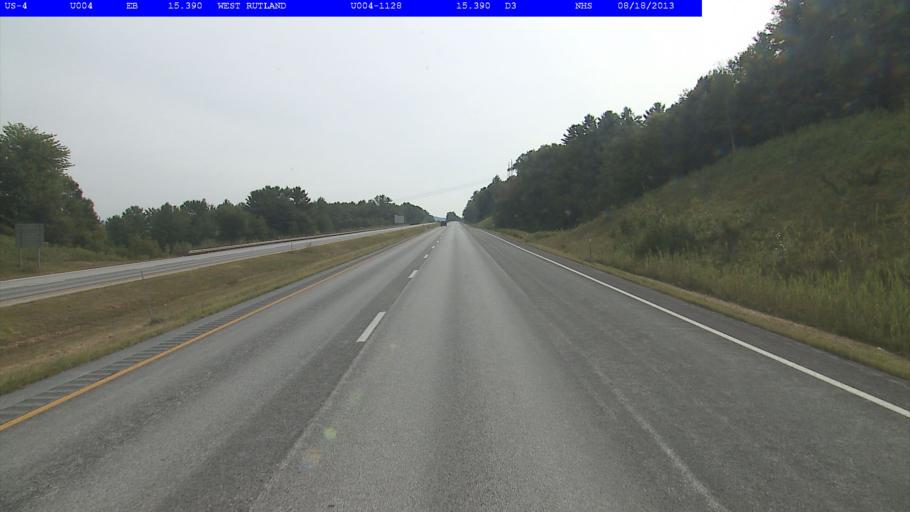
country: US
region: Vermont
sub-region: Rutland County
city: West Rutland
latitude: 43.5902
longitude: -73.0305
